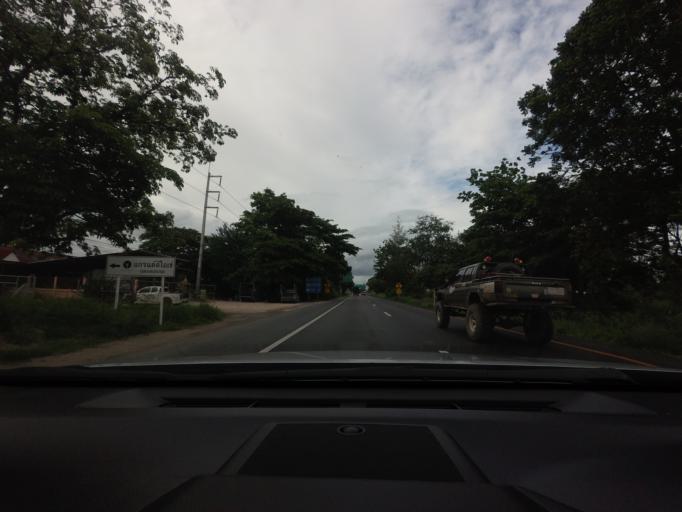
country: TH
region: Phetchaburi
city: Cha-am
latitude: 12.7159
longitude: 99.9181
